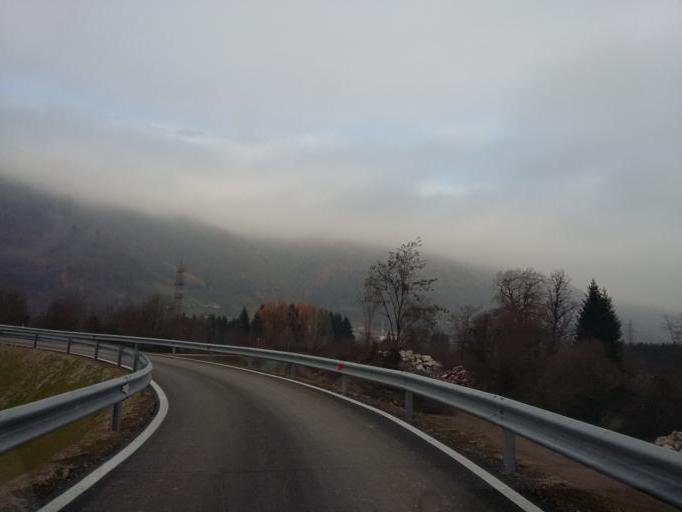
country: IT
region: Trentino-Alto Adige
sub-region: Provincia di Trento
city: Lodrone-Darzo
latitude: 45.8308
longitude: 10.5527
